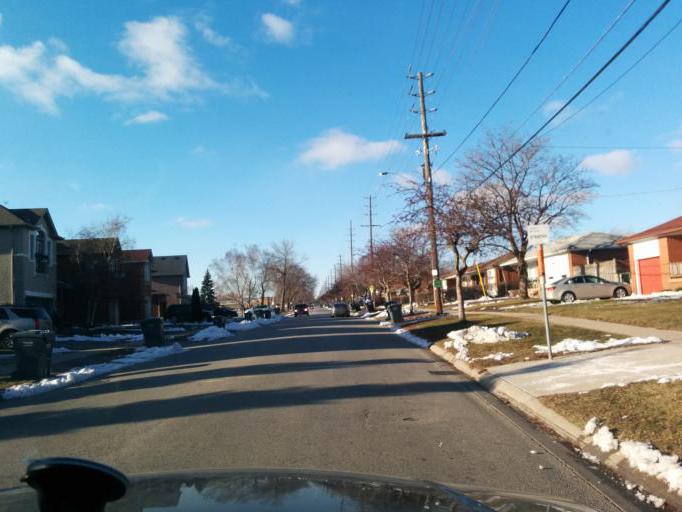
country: CA
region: Ontario
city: Etobicoke
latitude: 43.5835
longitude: -79.5677
